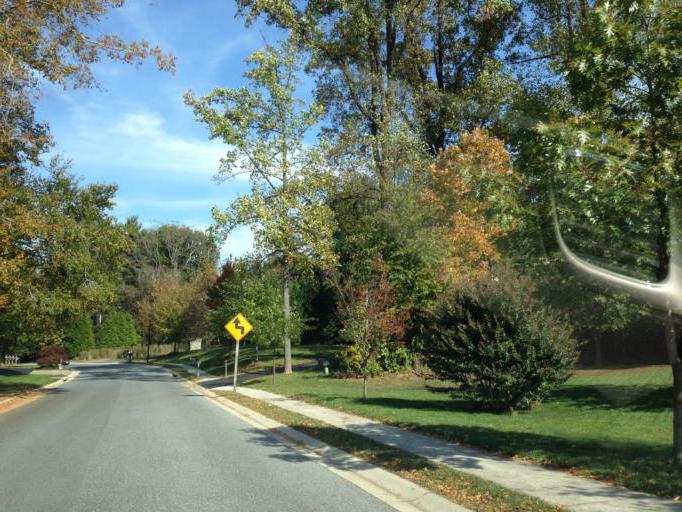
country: US
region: Maryland
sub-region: Howard County
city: Ellicott City
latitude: 39.2477
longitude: -76.8034
